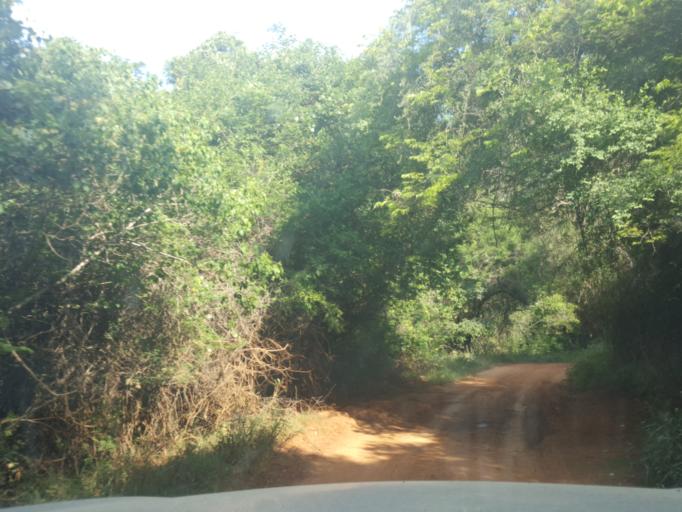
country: ZA
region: Limpopo
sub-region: Mopani District Municipality
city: Hoedspruit
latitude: -24.5939
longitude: 30.8261
